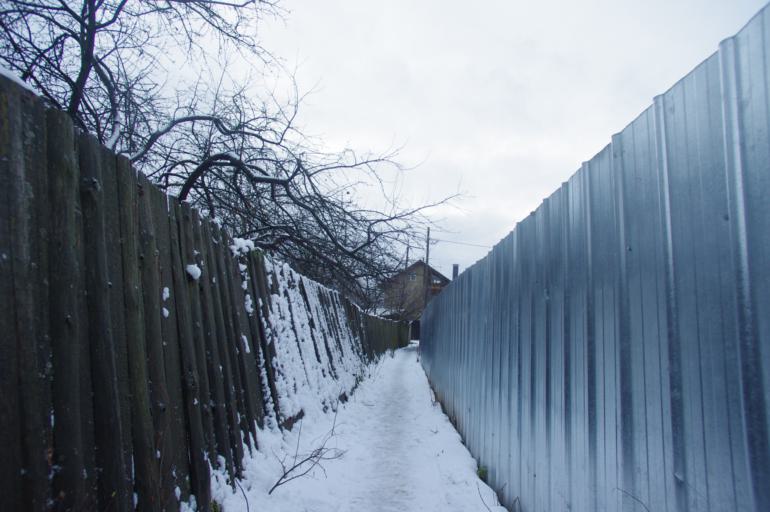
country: RU
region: Moskovskaya
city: Pavshino
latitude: 55.8131
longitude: 37.3528
